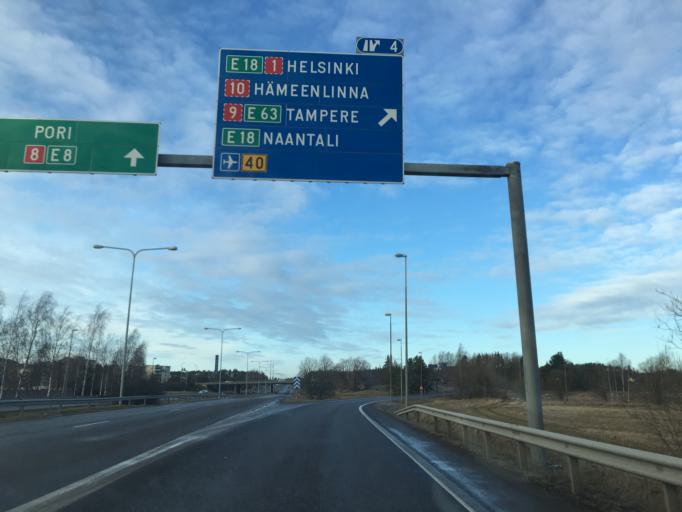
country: FI
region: Varsinais-Suomi
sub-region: Turku
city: Raisio
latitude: 60.4855
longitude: 22.1785
